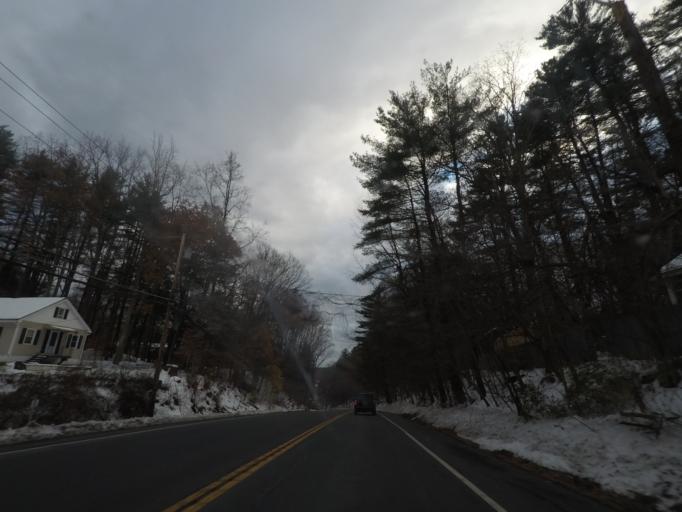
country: US
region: New York
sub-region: Ulster County
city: Rosendale Village
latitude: 41.8537
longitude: -74.0738
